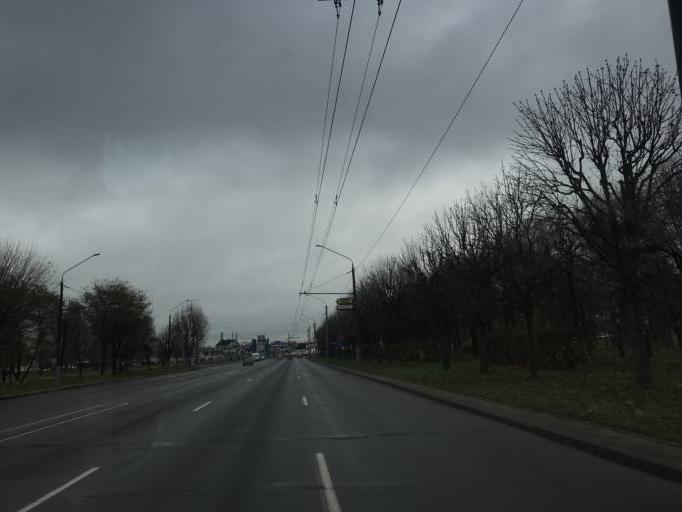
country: BY
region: Mogilev
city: Mahilyow
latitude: 53.8635
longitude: 30.3343
